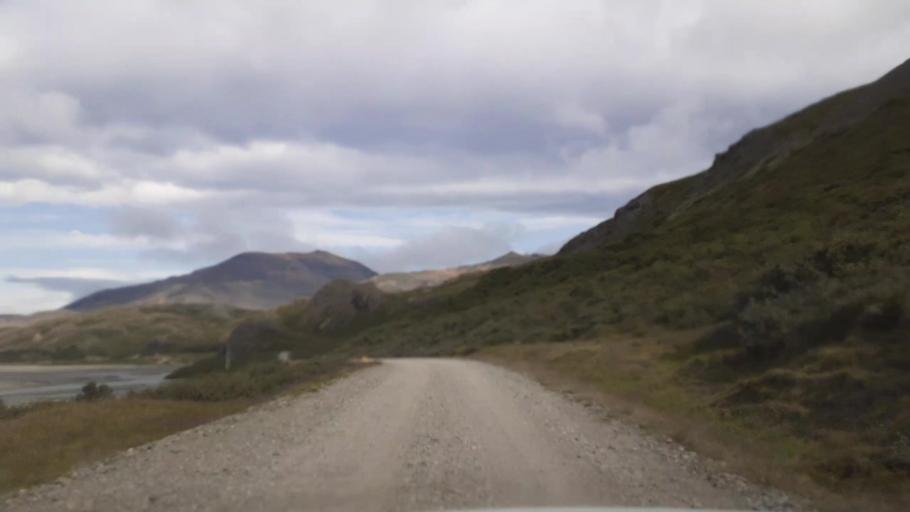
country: IS
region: East
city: Hoefn
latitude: 64.4242
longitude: -14.8813
